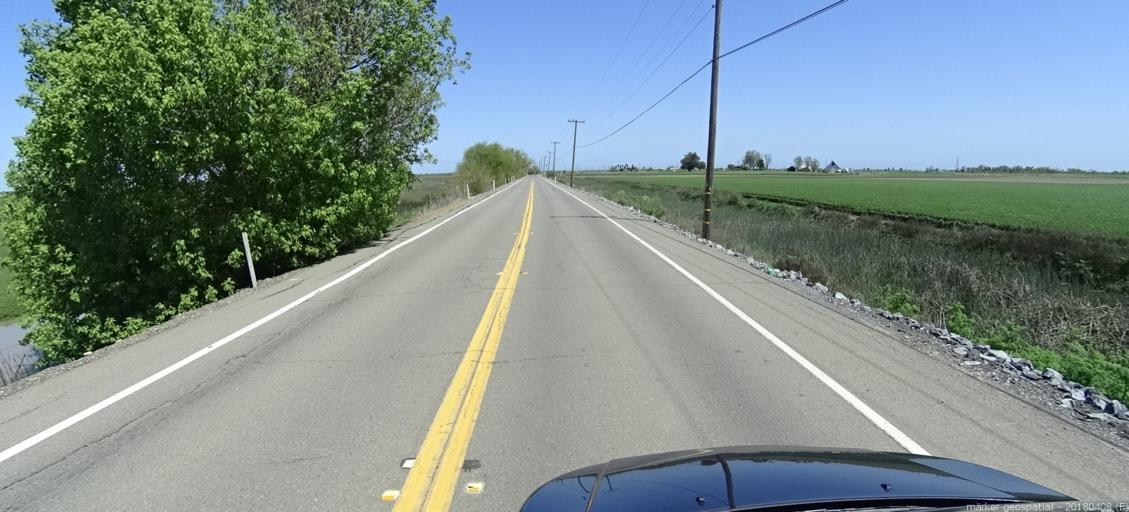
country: US
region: California
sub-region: Sacramento County
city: Laguna
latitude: 38.3663
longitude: -121.5068
